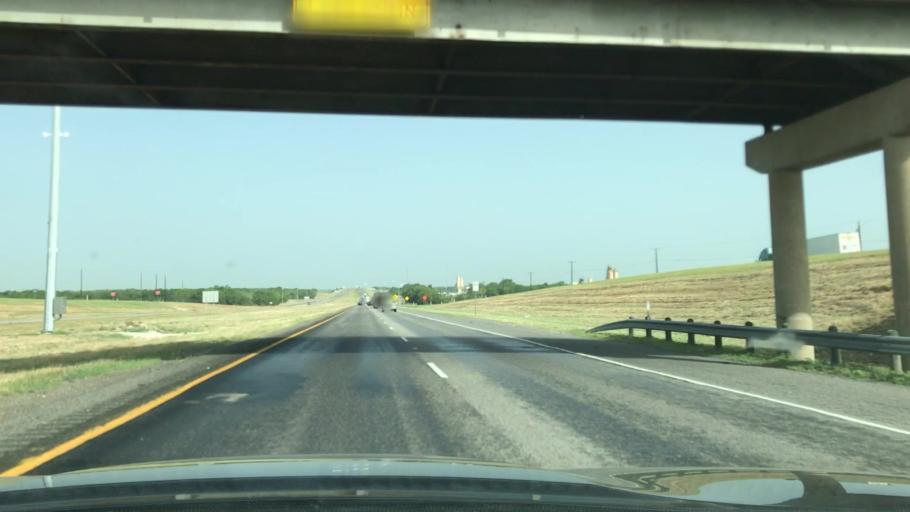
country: US
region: Texas
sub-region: Kaufman County
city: Terrell
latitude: 32.7300
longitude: -96.3399
